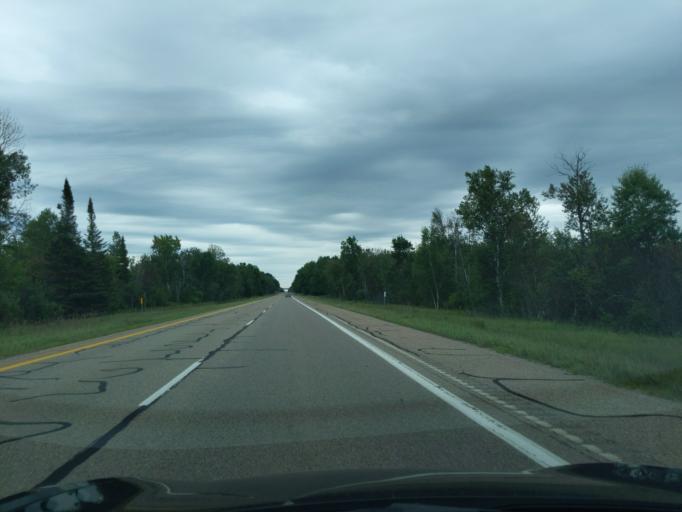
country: US
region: Michigan
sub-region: Roscommon County
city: Houghton Lake
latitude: 44.2095
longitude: -84.7969
